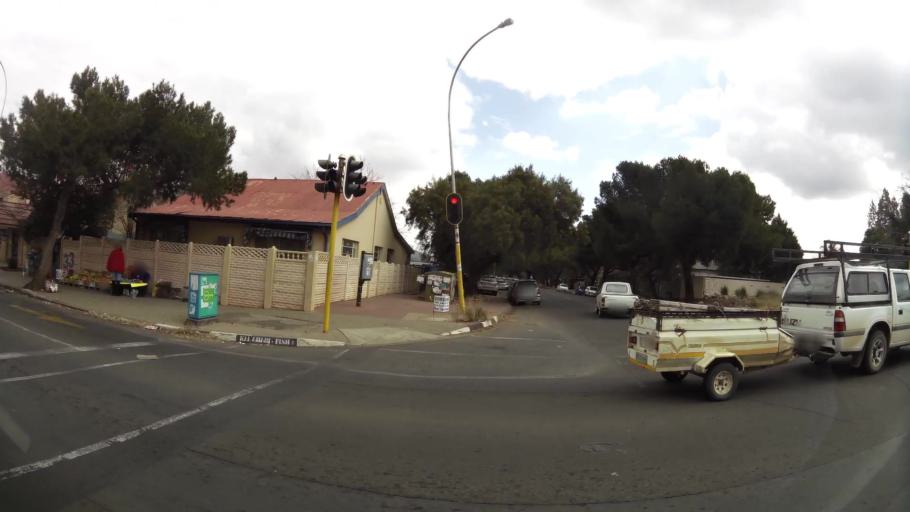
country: ZA
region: Orange Free State
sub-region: Mangaung Metropolitan Municipality
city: Bloemfontein
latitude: -29.1103
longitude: 26.2130
